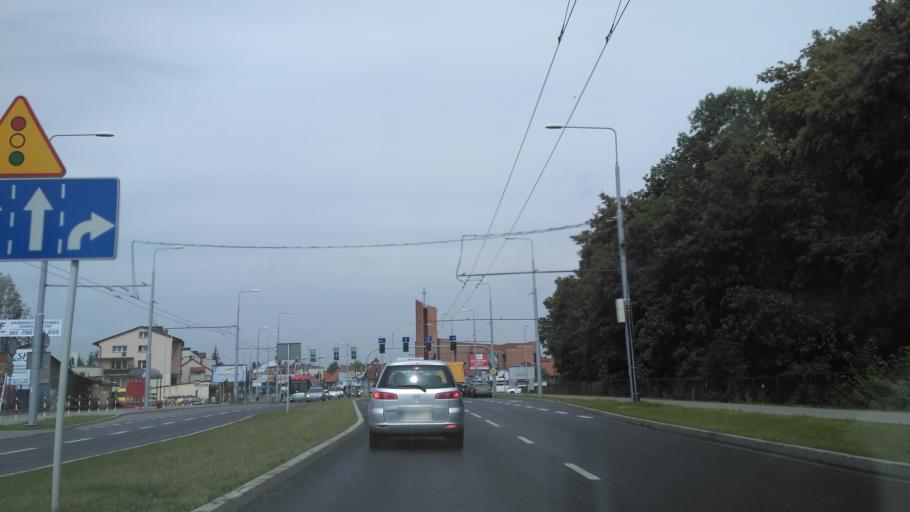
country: PL
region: Lublin Voivodeship
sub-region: Powiat lubelski
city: Lublin
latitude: 51.2065
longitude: 22.5867
